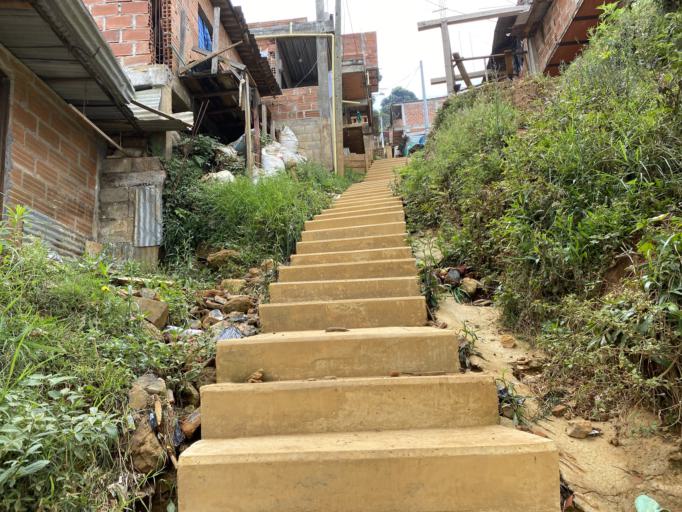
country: CO
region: Antioquia
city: Medellin
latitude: 6.2666
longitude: -75.5394
